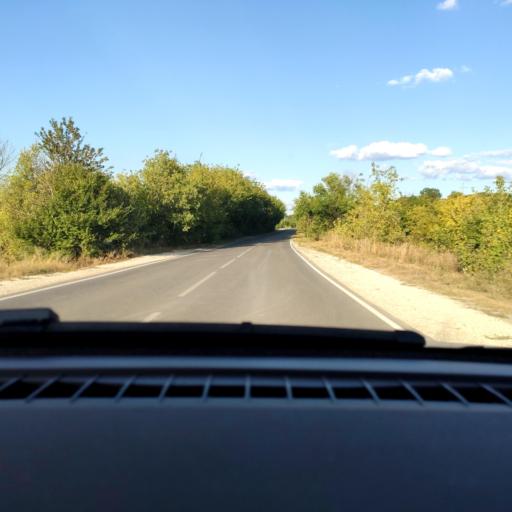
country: RU
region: Voronezj
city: Semiluki
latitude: 51.6597
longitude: 39.0036
